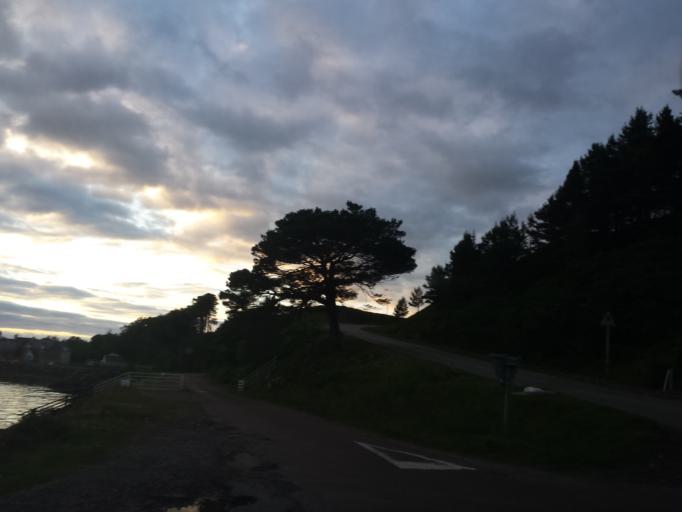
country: GB
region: Scotland
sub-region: Highland
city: Portree
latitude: 57.5180
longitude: -5.6485
